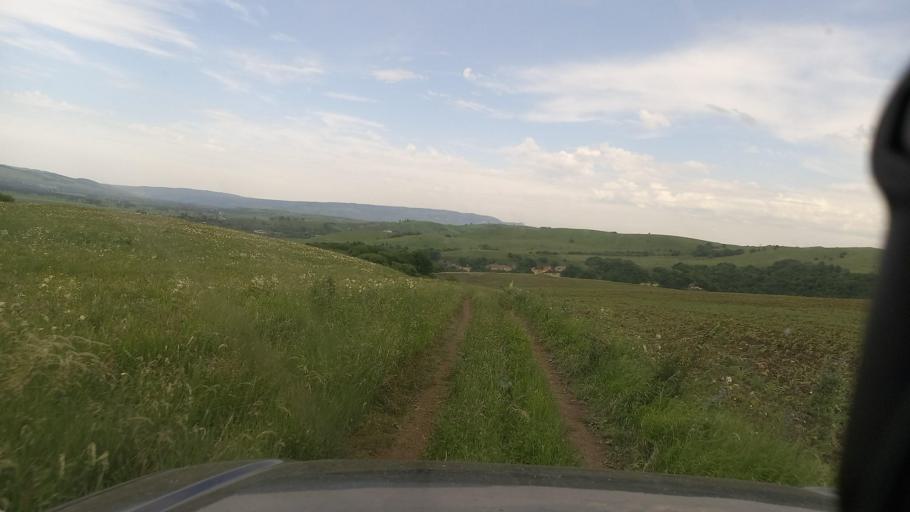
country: RU
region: Krasnodarskiy
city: Peredovaya
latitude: 44.0789
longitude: 41.3432
